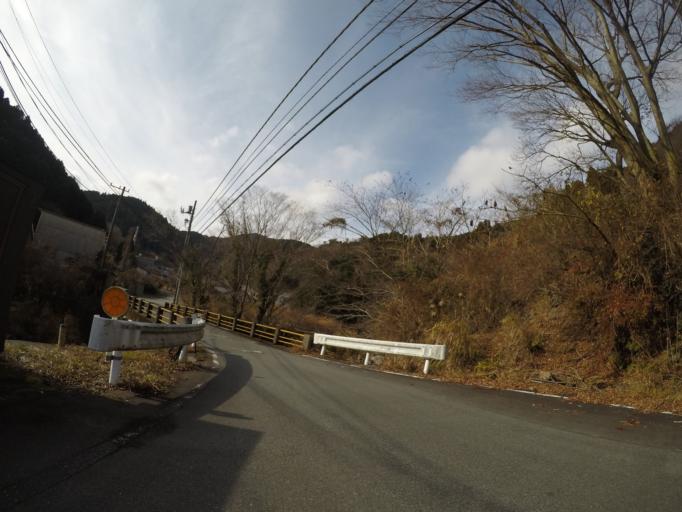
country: JP
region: Shizuoka
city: Heda
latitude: 34.8881
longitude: 138.8654
